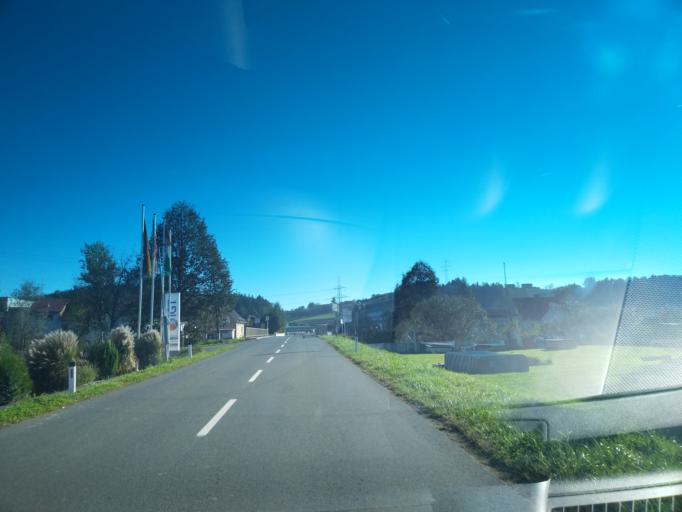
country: AT
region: Styria
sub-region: Politischer Bezirk Deutschlandsberg
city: Gross Sankt Florian
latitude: 46.8187
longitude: 15.3159
